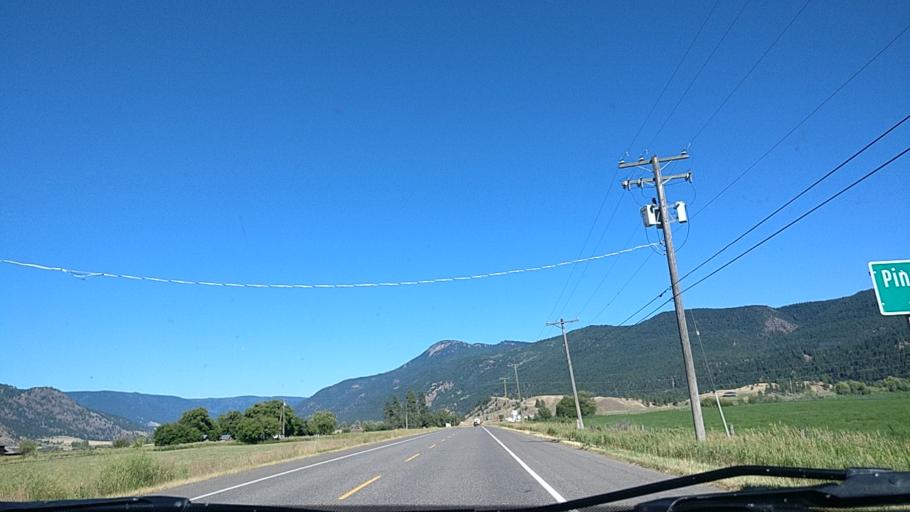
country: CA
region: British Columbia
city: Chase
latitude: 50.4612
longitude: -119.7300
